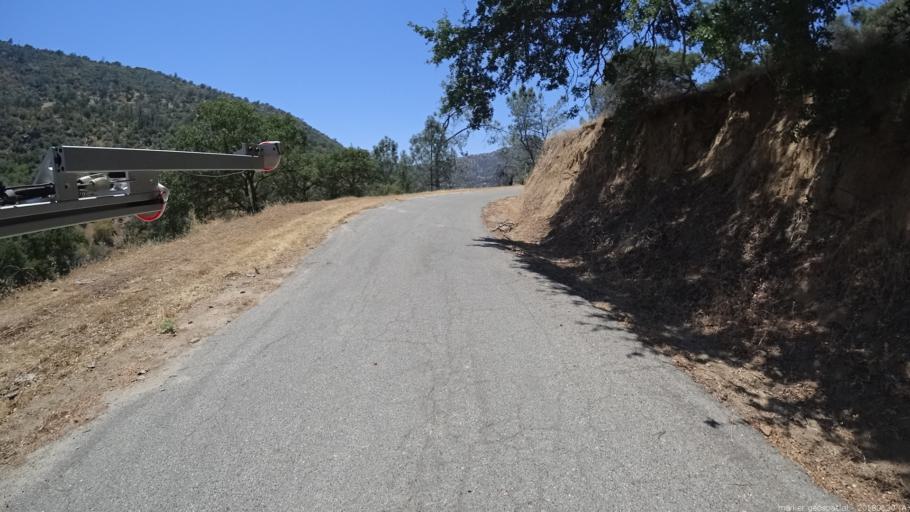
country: US
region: California
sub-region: Fresno County
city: Auberry
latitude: 37.1638
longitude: -119.4131
